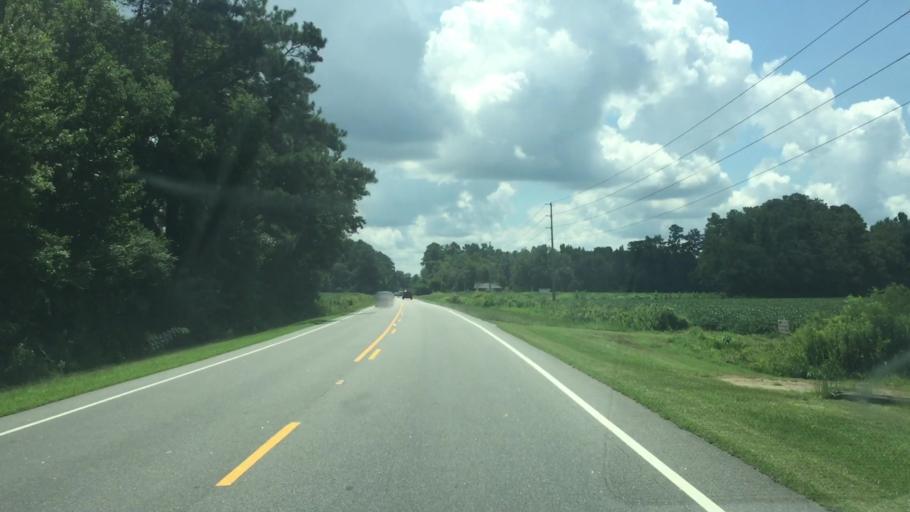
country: US
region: North Carolina
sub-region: Columbus County
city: Chadbourn
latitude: 34.3520
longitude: -78.8290
